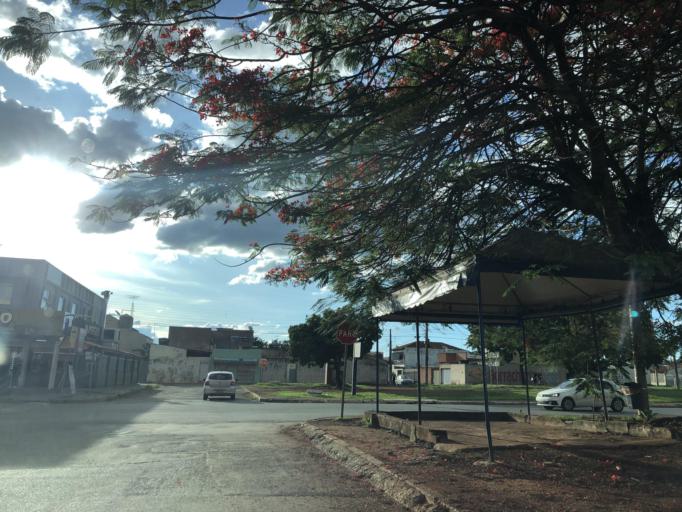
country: BR
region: Goias
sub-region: Luziania
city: Luziania
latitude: -16.0278
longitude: -48.0605
